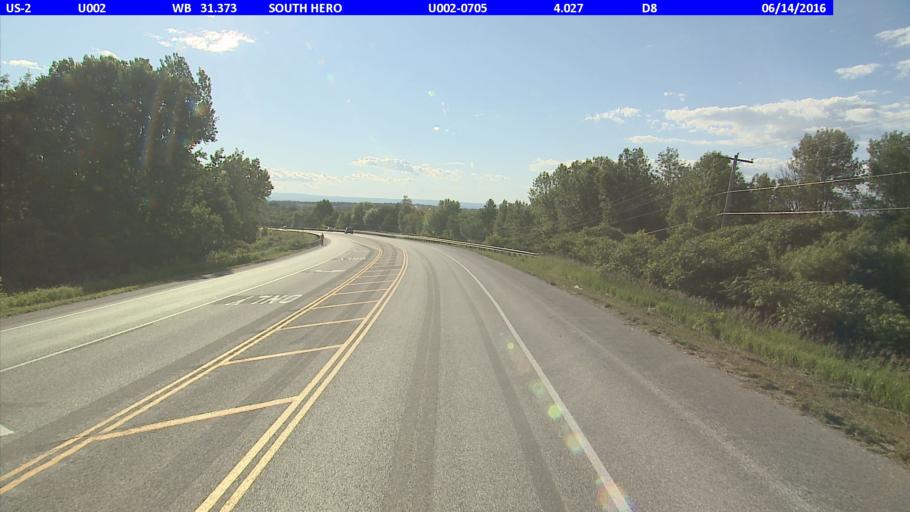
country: US
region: New York
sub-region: Clinton County
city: Cumberland Head
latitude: 44.6463
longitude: -73.2837
